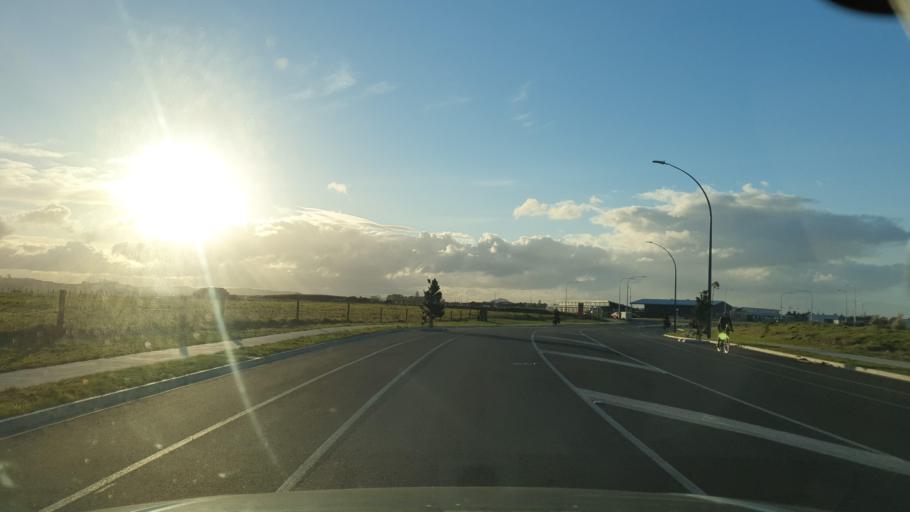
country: NZ
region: Bay of Plenty
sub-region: Western Bay of Plenty District
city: Maketu
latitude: -37.7237
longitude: 176.3219
